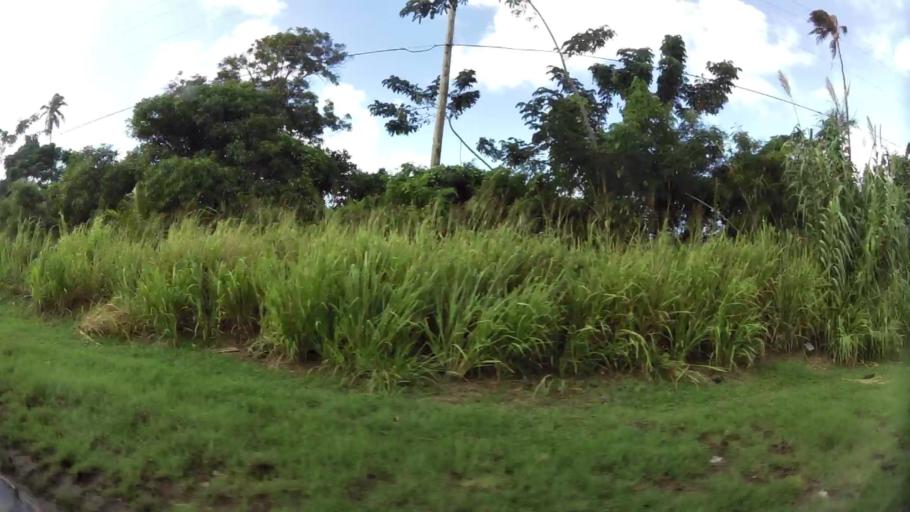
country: AG
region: Saint Mary
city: Bolands
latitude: 17.0712
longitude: -61.8679
